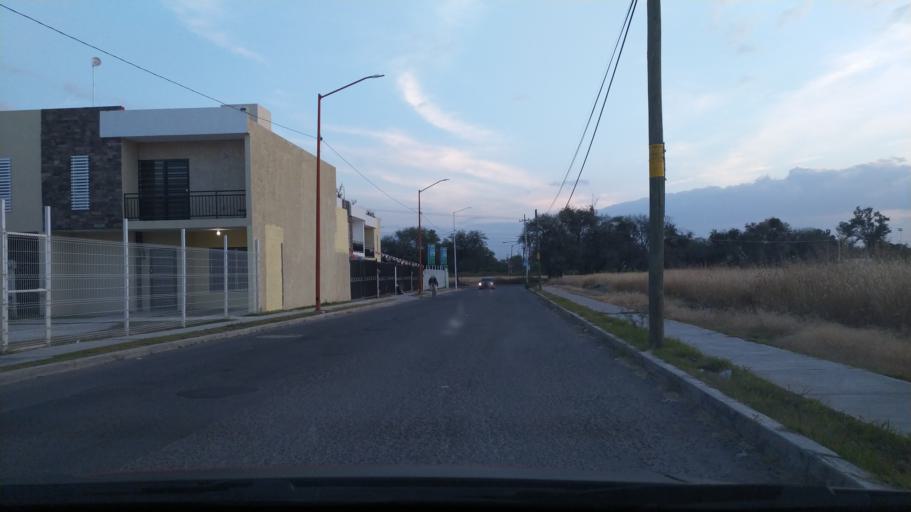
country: MX
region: Guanajuato
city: San Francisco del Rincon
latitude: 21.0339
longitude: -101.8485
